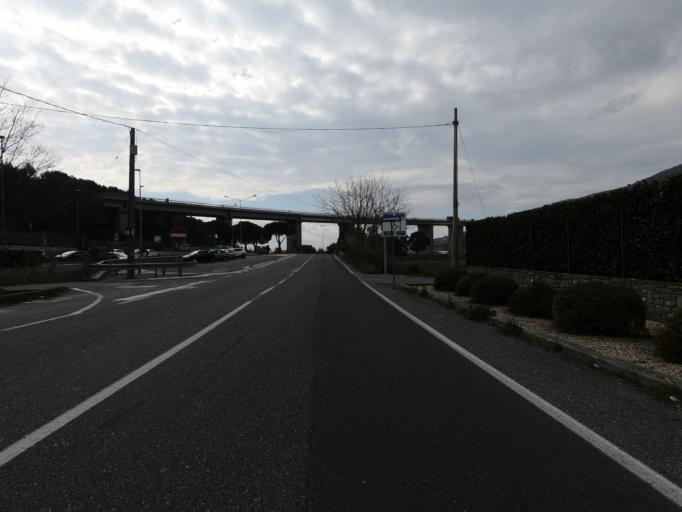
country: IT
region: Liguria
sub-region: Provincia di Savona
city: Andora
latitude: 43.9669
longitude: 8.1415
